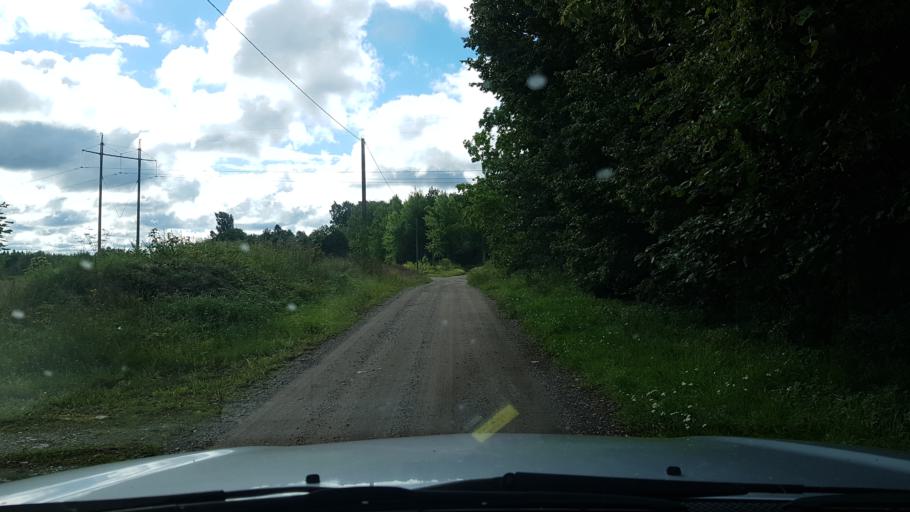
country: EE
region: Harju
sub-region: Rae vald
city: Vaida
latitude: 59.2694
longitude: 25.0265
